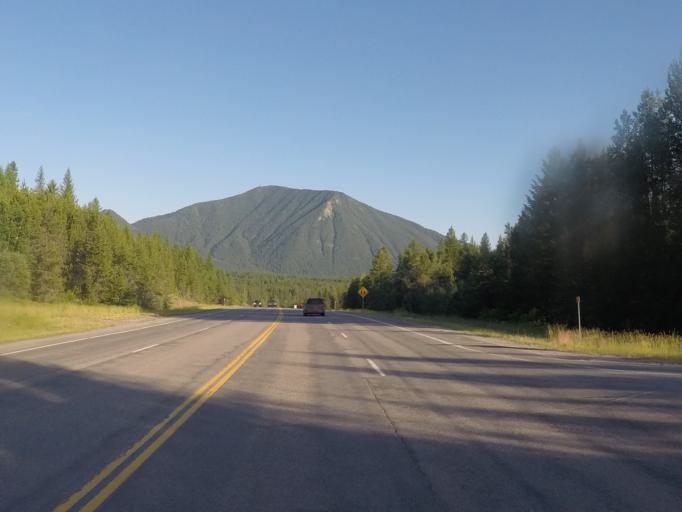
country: US
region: Montana
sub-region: Flathead County
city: Columbia Falls
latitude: 48.4759
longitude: -114.0007
